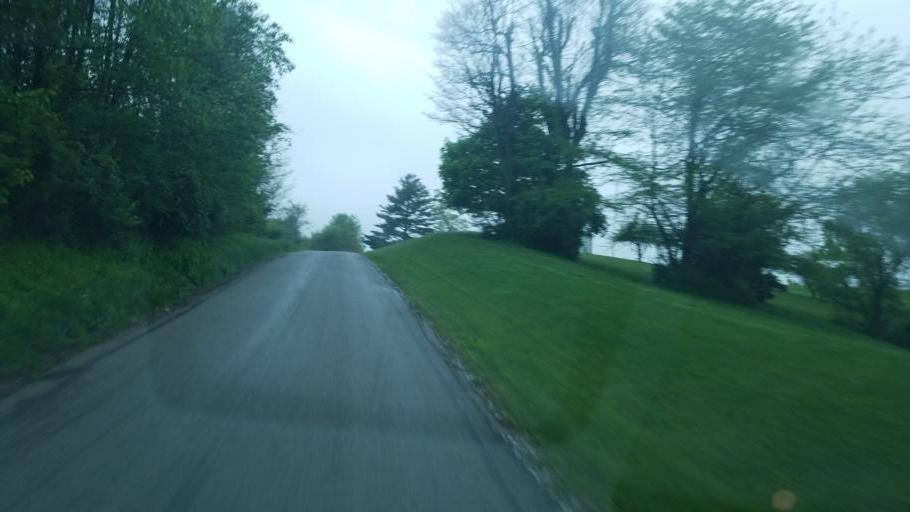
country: US
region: Ohio
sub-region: Highland County
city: Hillsboro
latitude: 39.1777
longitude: -83.6460
